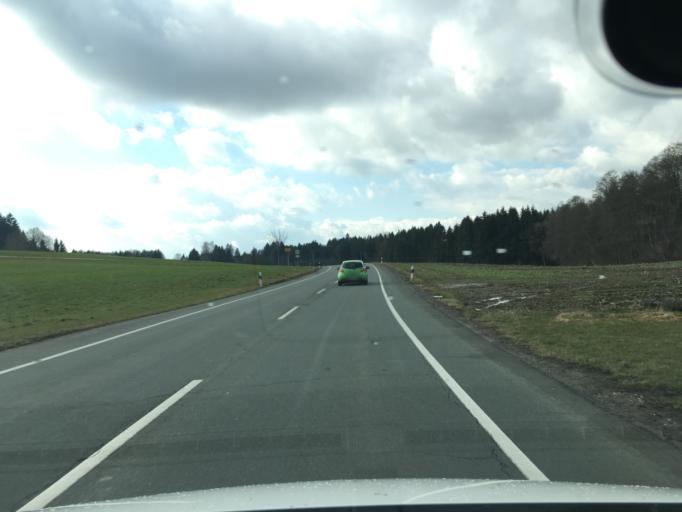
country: DE
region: Bavaria
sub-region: Upper Bavaria
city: Riedering
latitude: 47.8366
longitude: 12.1946
